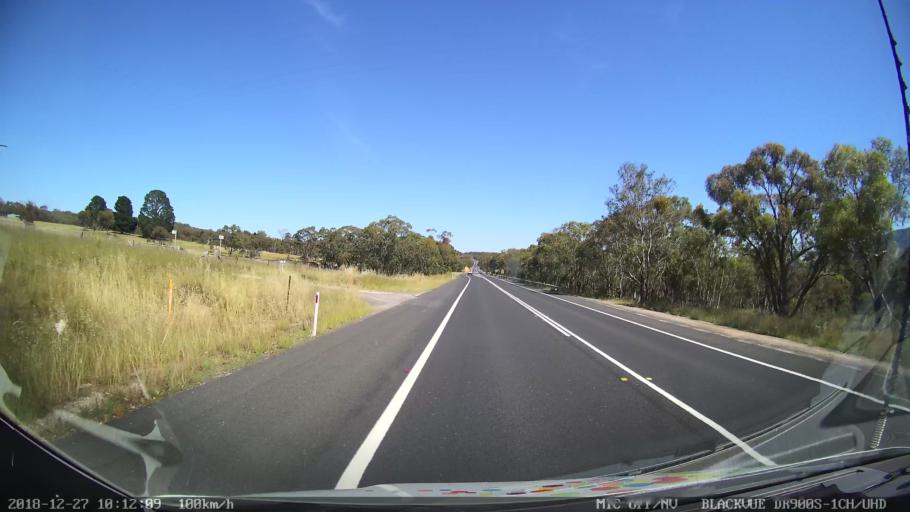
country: AU
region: New South Wales
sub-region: Bathurst Regional
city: Kelso
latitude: -33.4463
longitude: 149.7639
